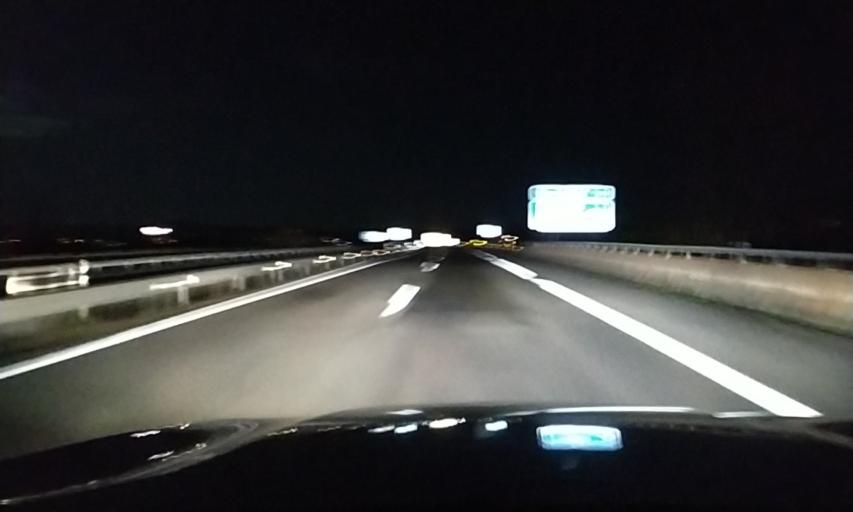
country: ES
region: Galicia
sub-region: Provincia de Ourense
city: Xinzo de Limia
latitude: 42.0606
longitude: -7.6775
